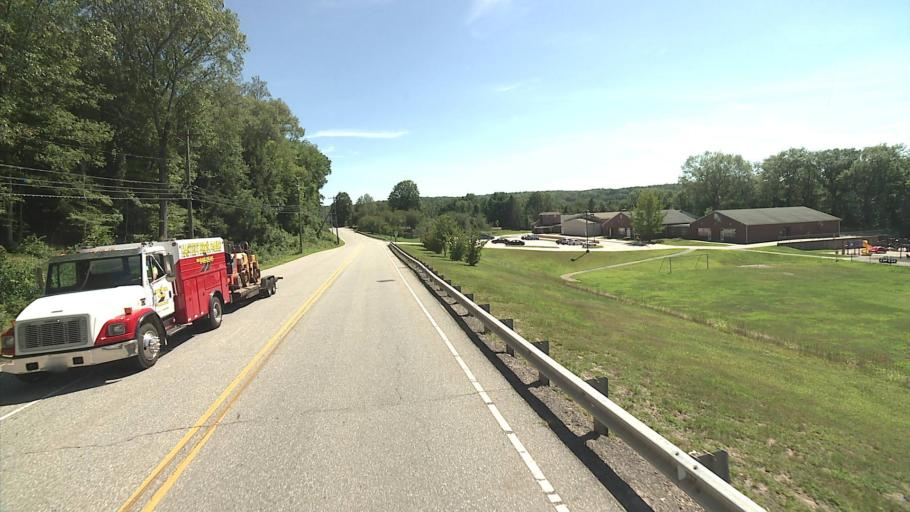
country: US
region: Connecticut
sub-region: New London County
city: Baltic
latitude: 41.6244
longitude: -72.0851
